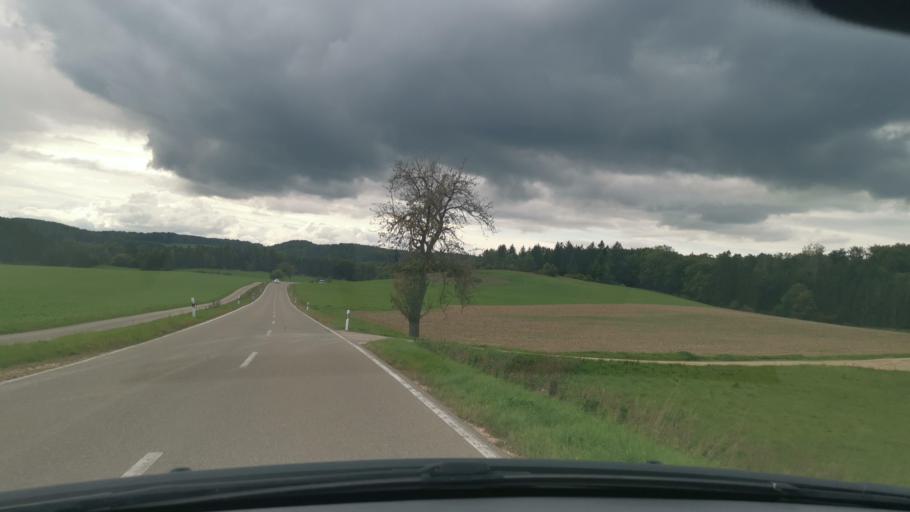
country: DE
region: Baden-Wuerttemberg
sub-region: Tuebingen Region
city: Lauterach
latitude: 48.3098
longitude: 9.6009
